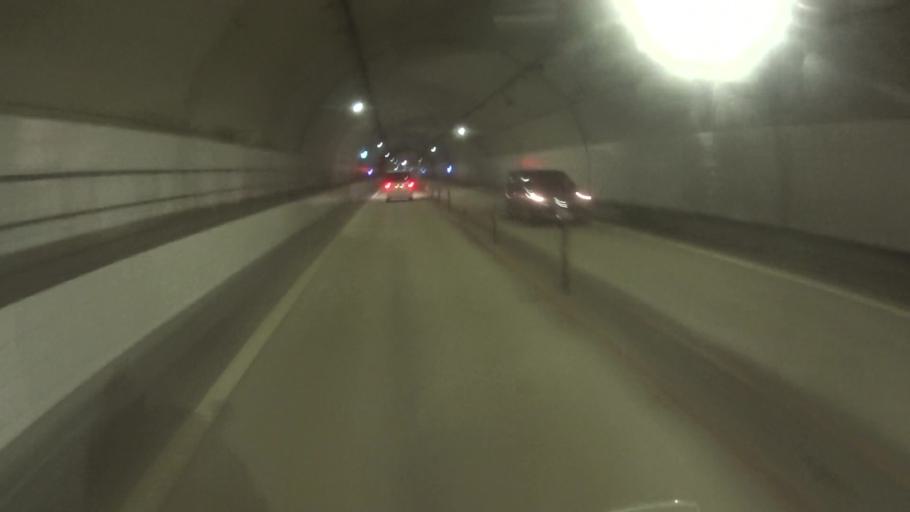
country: JP
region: Kyoto
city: Miyazu
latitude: 35.5261
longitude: 135.1768
